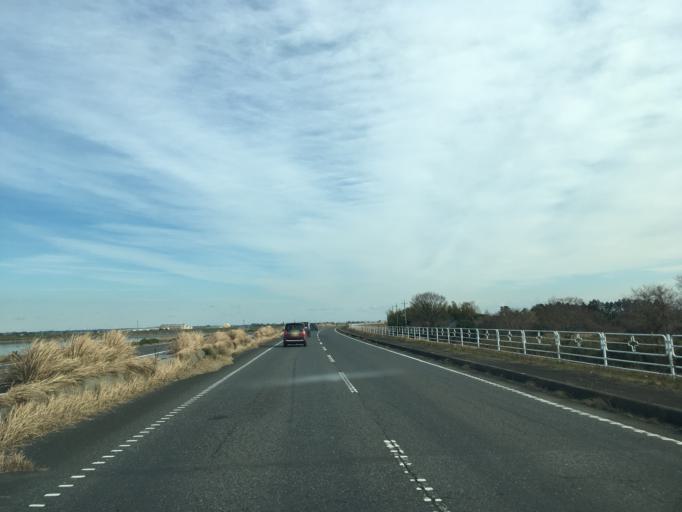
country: JP
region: Chiba
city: Katori-shi
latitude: 35.9149
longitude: 140.4547
